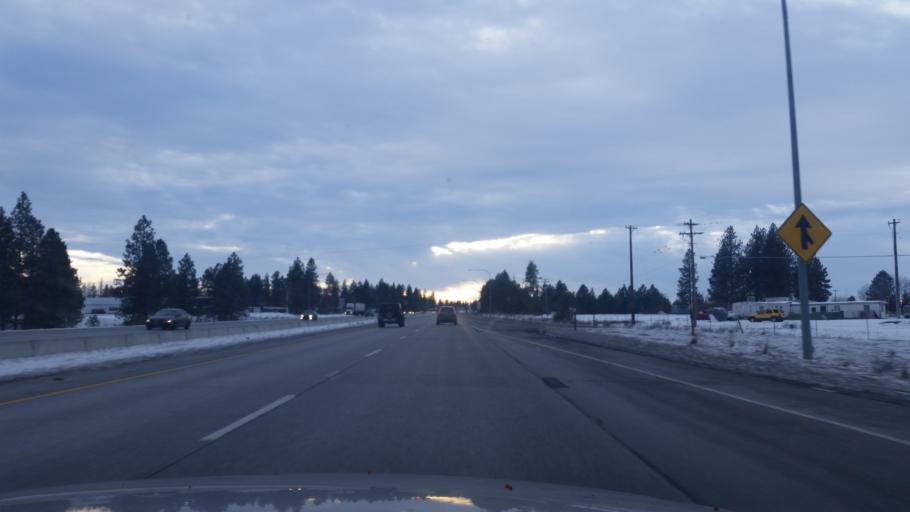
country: US
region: Washington
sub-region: Spokane County
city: Spokane
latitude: 47.6197
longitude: -117.5039
